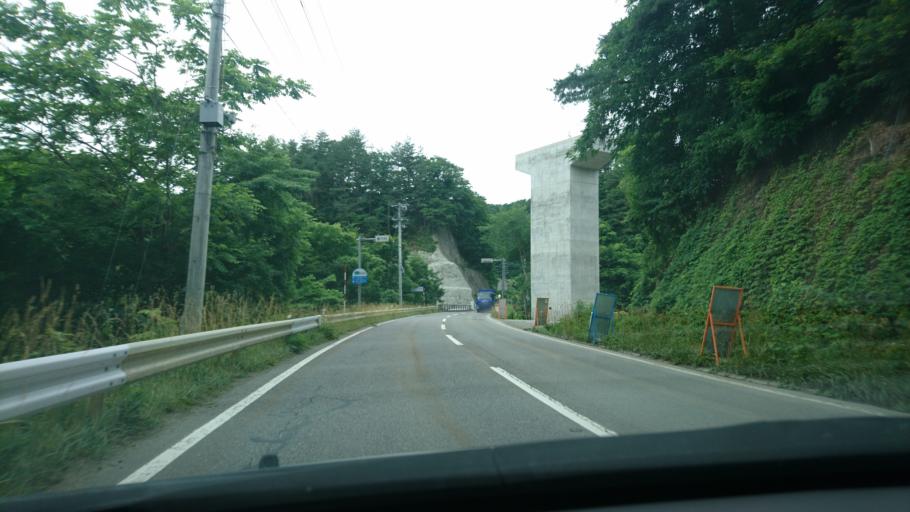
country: JP
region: Iwate
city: Miyako
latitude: 39.9760
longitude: 141.8584
